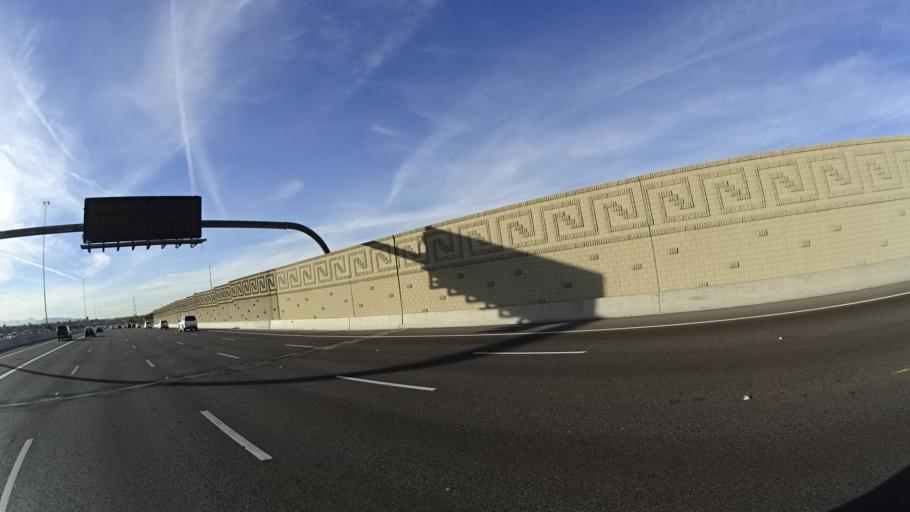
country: US
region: Arizona
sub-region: Maricopa County
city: Gilbert
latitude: 33.3864
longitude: -111.7384
